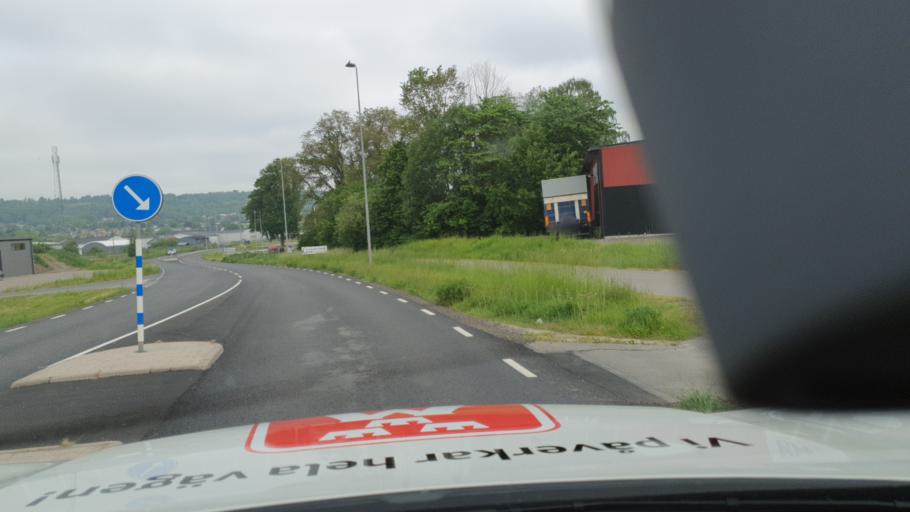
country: SE
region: Vaestra Goetaland
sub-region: Falkopings Kommun
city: Falkoeping
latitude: 58.1619
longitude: 13.5471
